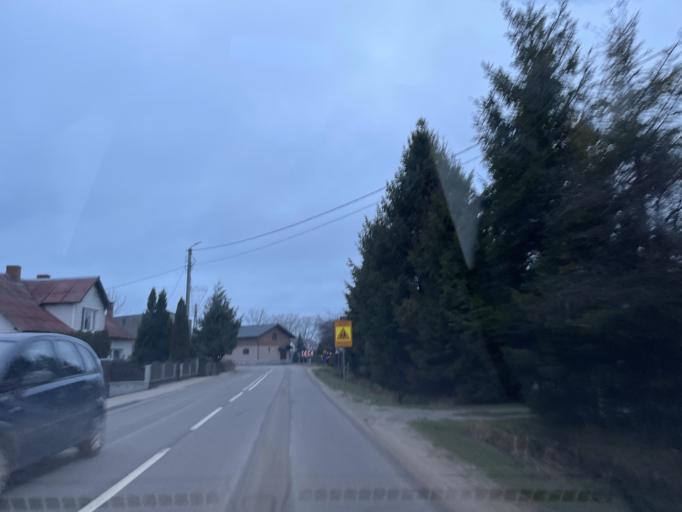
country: PL
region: Pomeranian Voivodeship
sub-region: Powiat wejherowski
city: Szemud
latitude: 54.4142
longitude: 18.2027
